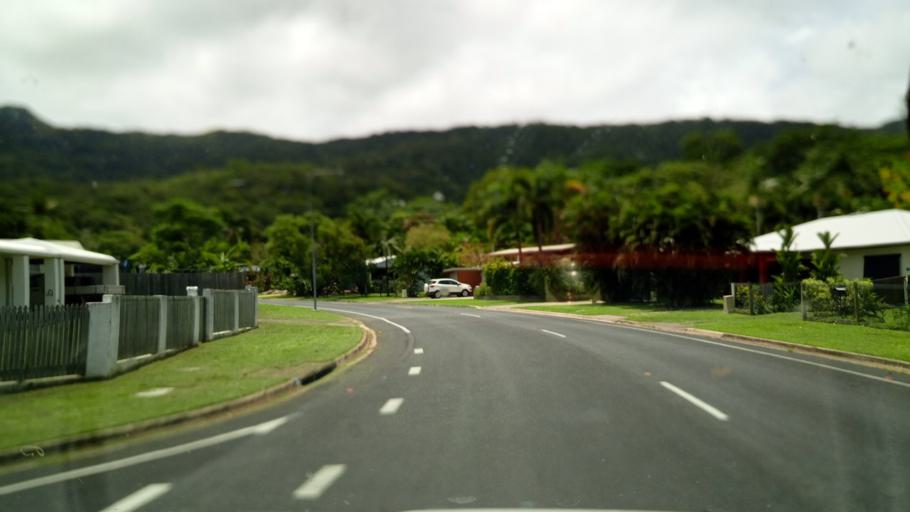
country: AU
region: Queensland
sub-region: Cairns
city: Yorkeys Knob
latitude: -16.8335
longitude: 145.6882
